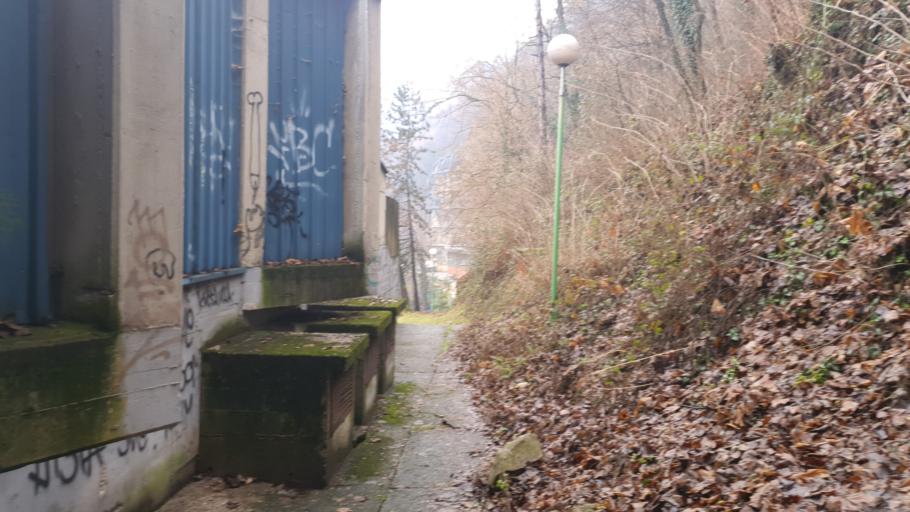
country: RS
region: Central Serbia
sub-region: Zlatiborski Okrug
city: Uzice
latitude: 43.8479
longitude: 19.8460
